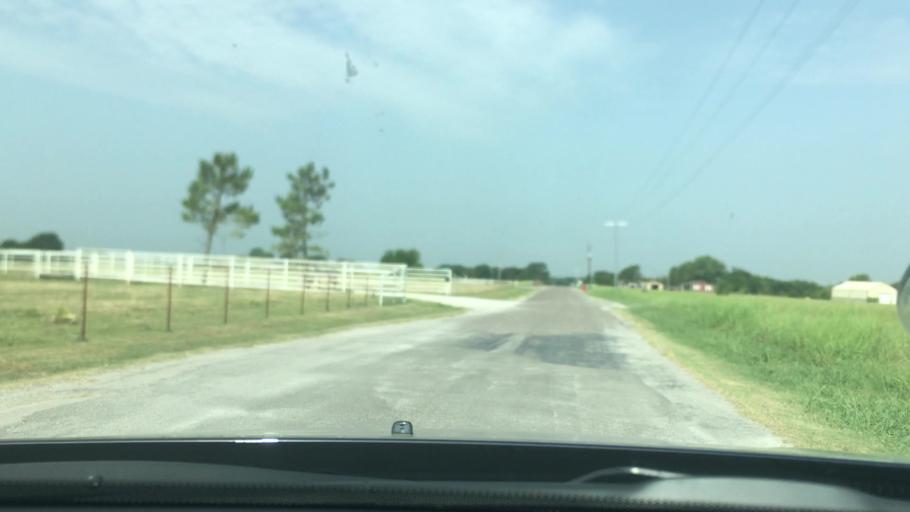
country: US
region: Oklahoma
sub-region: Garvin County
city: Pauls Valley
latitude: 34.7967
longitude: -97.1780
